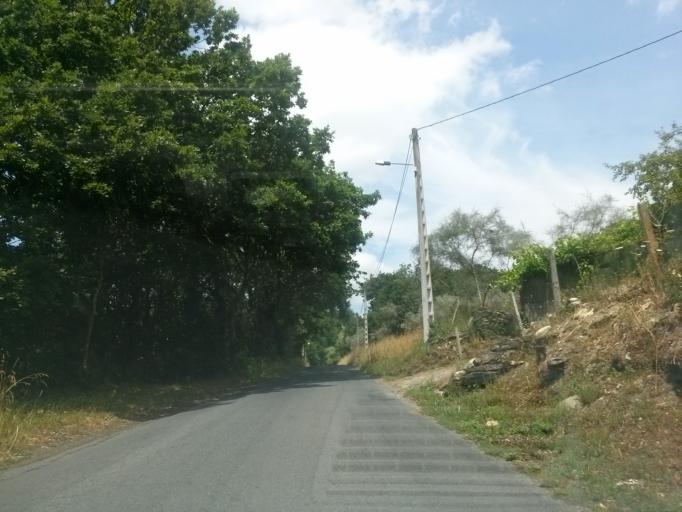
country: ES
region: Galicia
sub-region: Provincia de Lugo
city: Lugo
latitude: 43.0353
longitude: -7.5891
